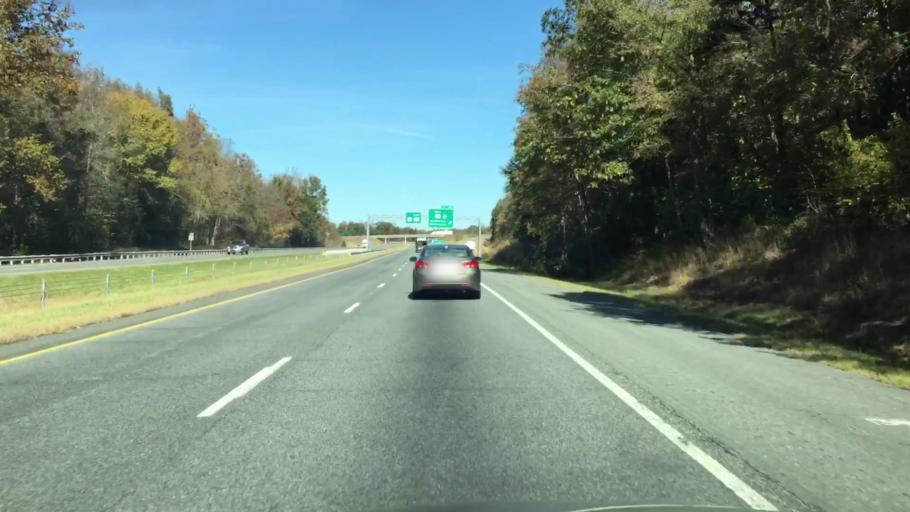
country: US
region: North Carolina
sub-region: Rockingham County
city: Reidsville
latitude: 36.3042
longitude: -79.6419
